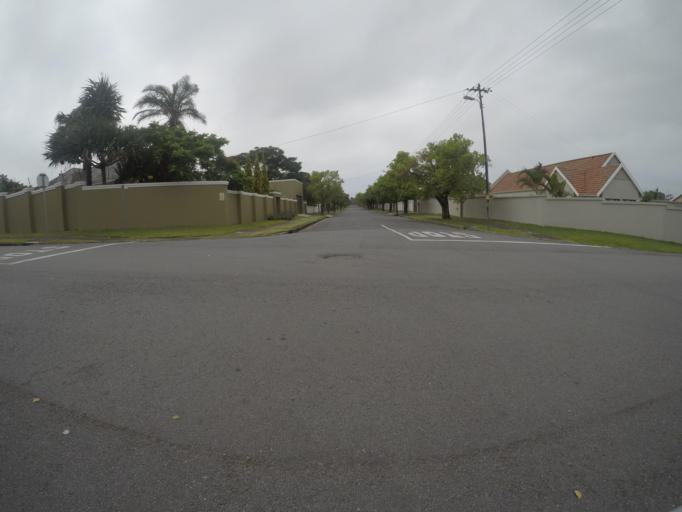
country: ZA
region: Eastern Cape
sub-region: Buffalo City Metropolitan Municipality
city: East London
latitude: -32.9875
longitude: 27.9297
